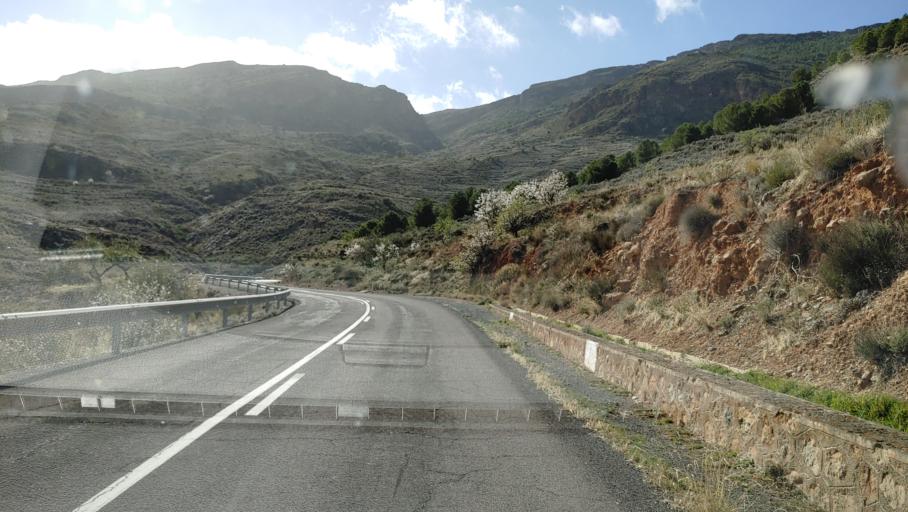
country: ES
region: Andalusia
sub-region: Provincia de Almeria
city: Alicun
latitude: 36.9376
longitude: -2.6052
